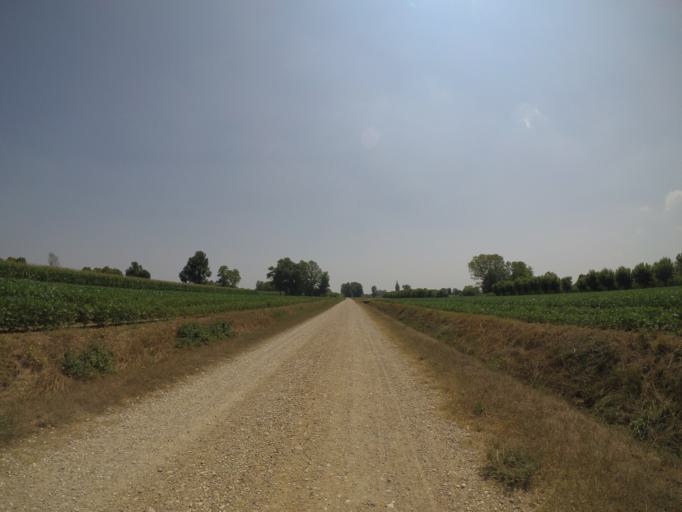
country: IT
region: Friuli Venezia Giulia
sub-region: Provincia di Udine
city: Talmassons
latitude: 45.9218
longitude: 13.1231
